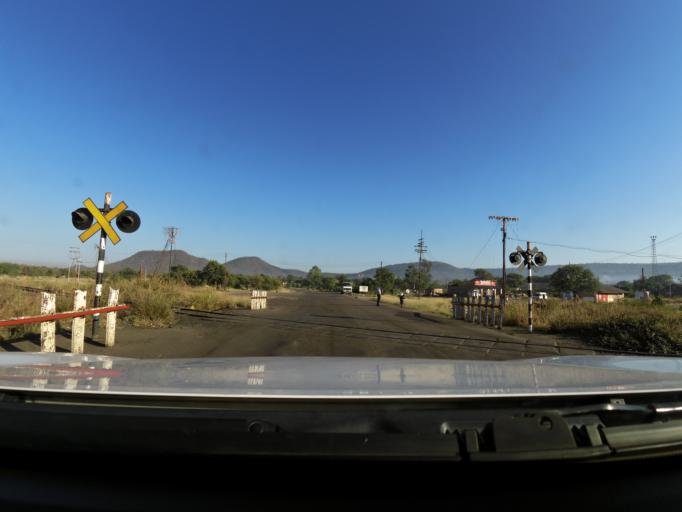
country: ZW
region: Matabeleland North
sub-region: Hwange District
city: Hwange
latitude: -18.3350
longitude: 26.4736
